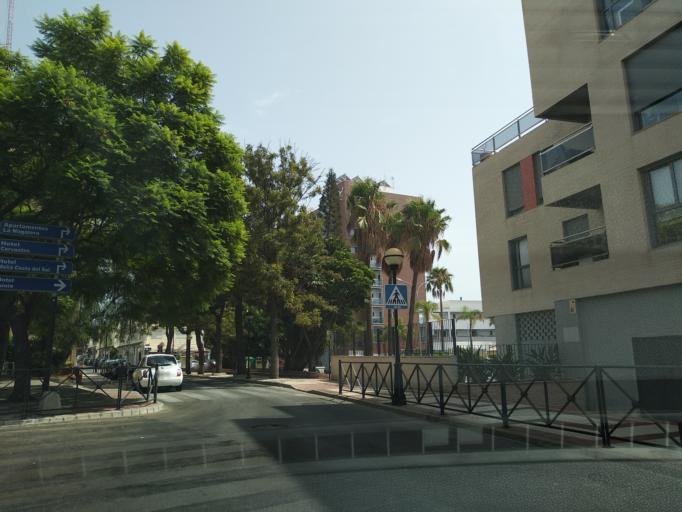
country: ES
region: Andalusia
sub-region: Provincia de Malaga
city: Torremolinos
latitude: 36.6185
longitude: -4.4998
